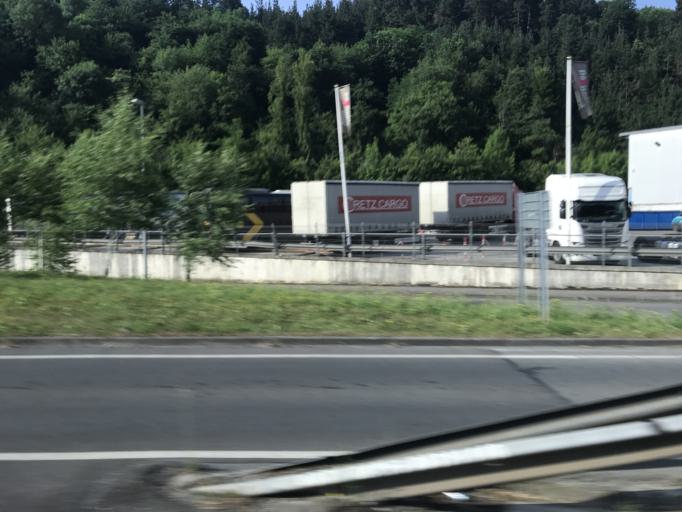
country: ES
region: Basque Country
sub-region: Provincia de Guipuzcoa
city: Beasain
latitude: 43.0448
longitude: -2.2007
